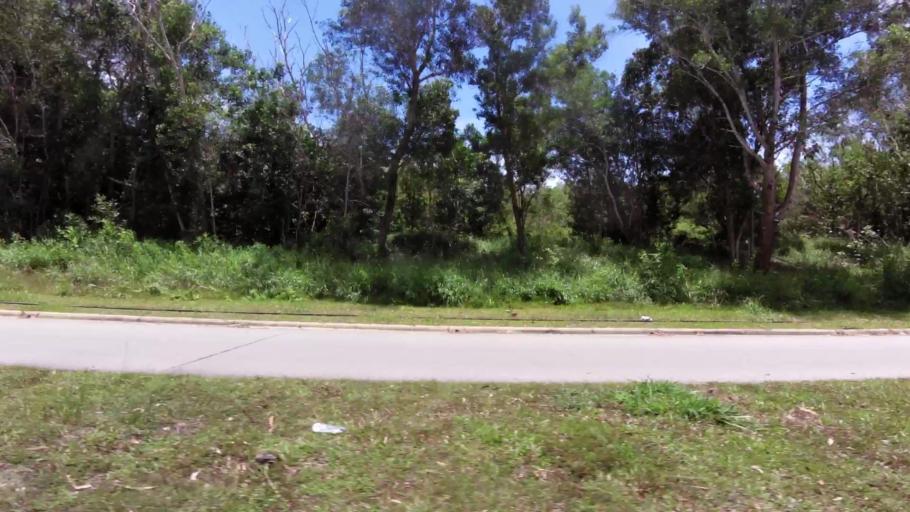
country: BN
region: Brunei and Muara
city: Bandar Seri Begawan
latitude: 4.9516
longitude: 114.8958
